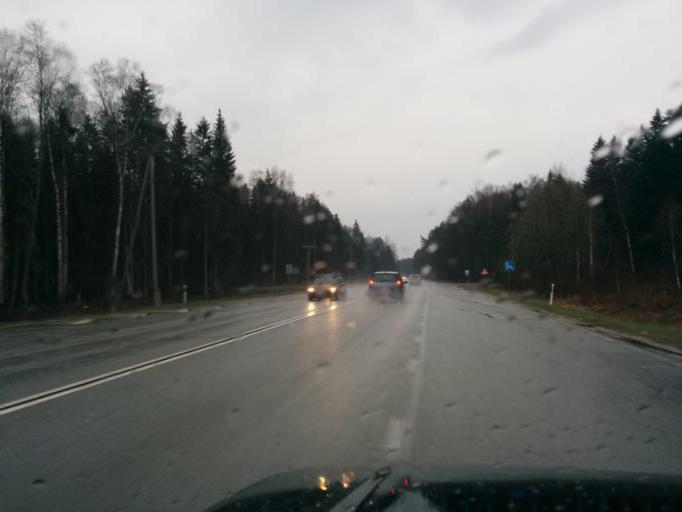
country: LV
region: Marupe
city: Marupe
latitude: 56.8315
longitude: 24.0457
